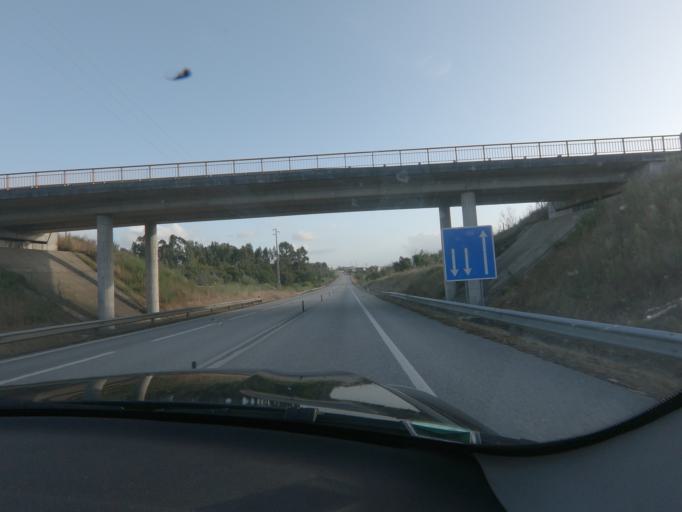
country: PT
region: Viseu
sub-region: Santa Comba Dao
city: Santa Comba Dao
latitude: 40.3681
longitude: -8.1305
